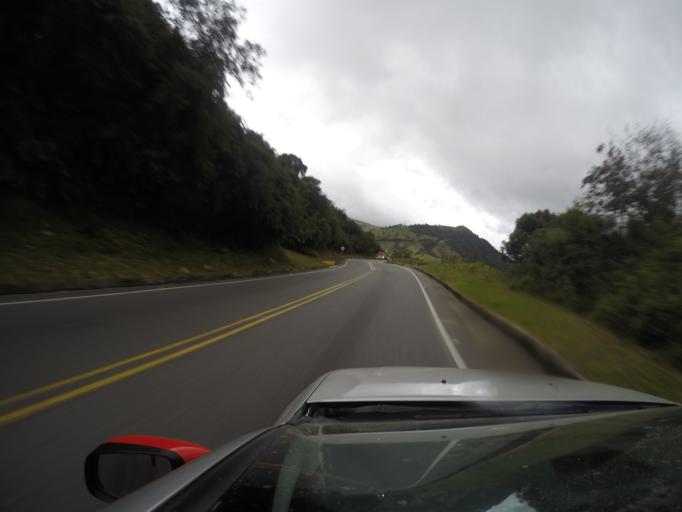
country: CO
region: Tolima
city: Herveo
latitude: 5.0655
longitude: -75.3096
